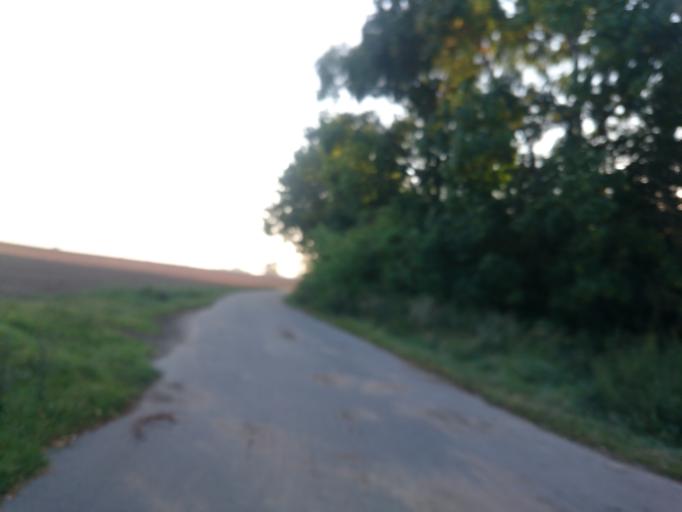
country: DE
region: Mecklenburg-Vorpommern
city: Barth
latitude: 54.3637
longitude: 12.7921
